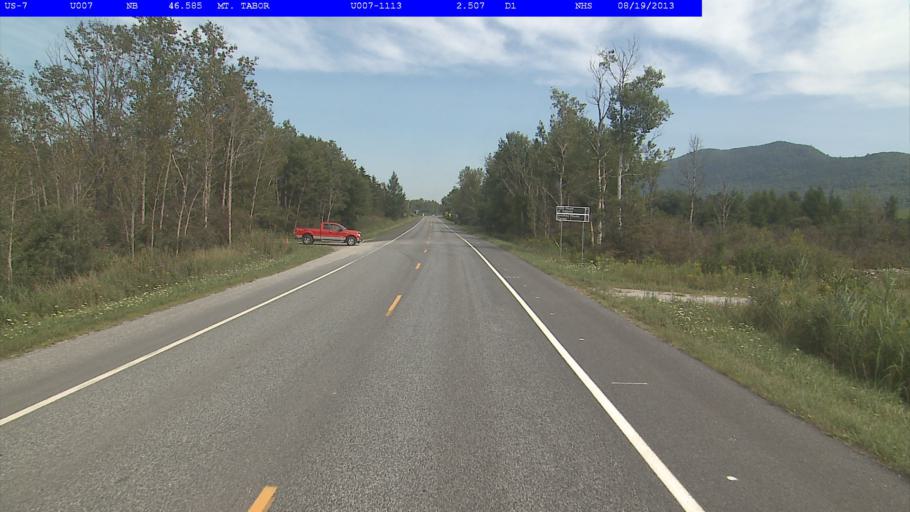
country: US
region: Vermont
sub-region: Bennington County
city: Manchester Center
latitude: 43.3412
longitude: -72.9920
